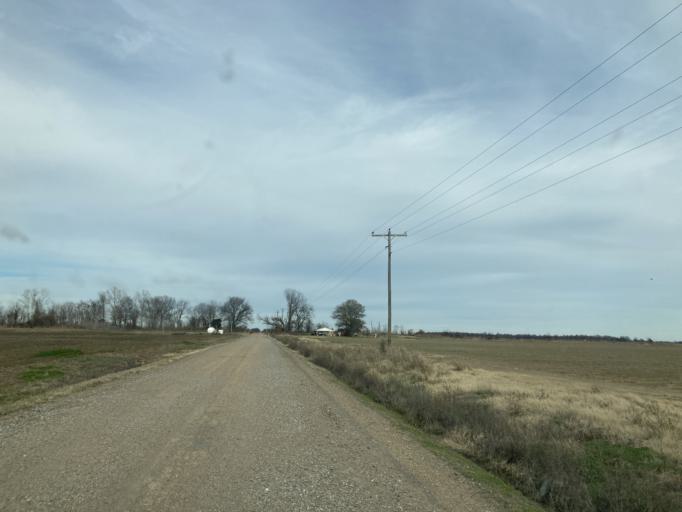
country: US
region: Mississippi
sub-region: Humphreys County
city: Belzoni
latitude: 33.1502
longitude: -90.6067
